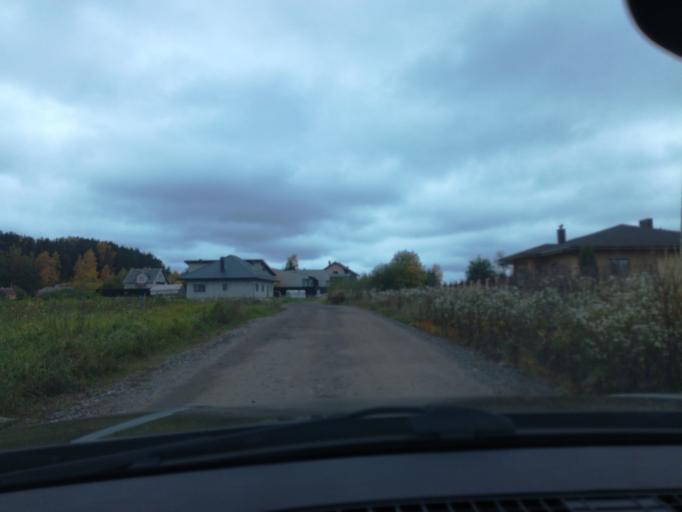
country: LT
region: Alytaus apskritis
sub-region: Alytus
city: Alytus
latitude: 54.4057
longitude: 24.0146
